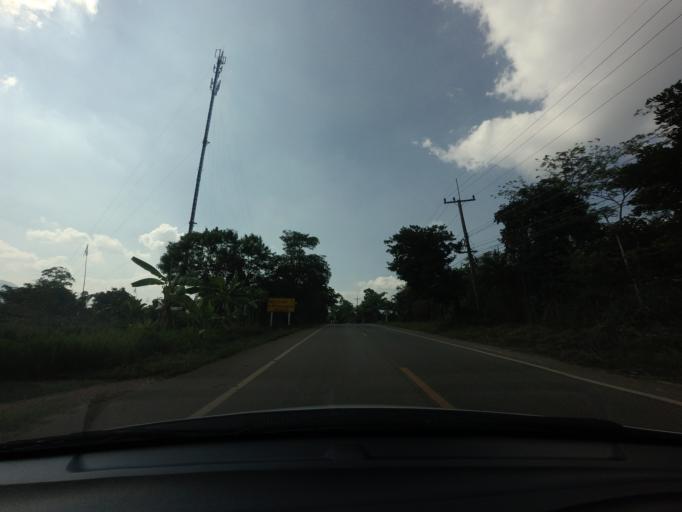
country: TH
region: Nakhon Ratchasima
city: Wang Nam Khiao
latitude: 14.4582
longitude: 101.6631
